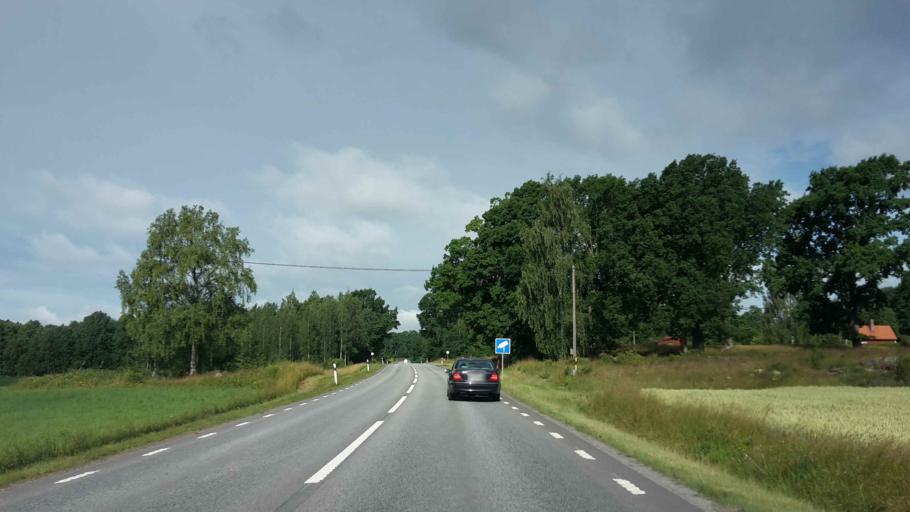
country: SE
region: OEstergoetland
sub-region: Motala Kommun
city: Borensberg
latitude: 58.5806
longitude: 15.1950
